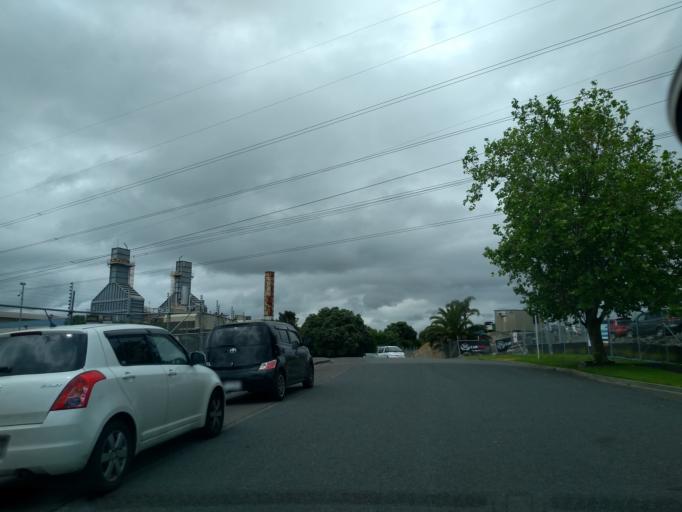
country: NZ
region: Auckland
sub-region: Auckland
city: Mangere
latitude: -36.9271
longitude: 174.8255
